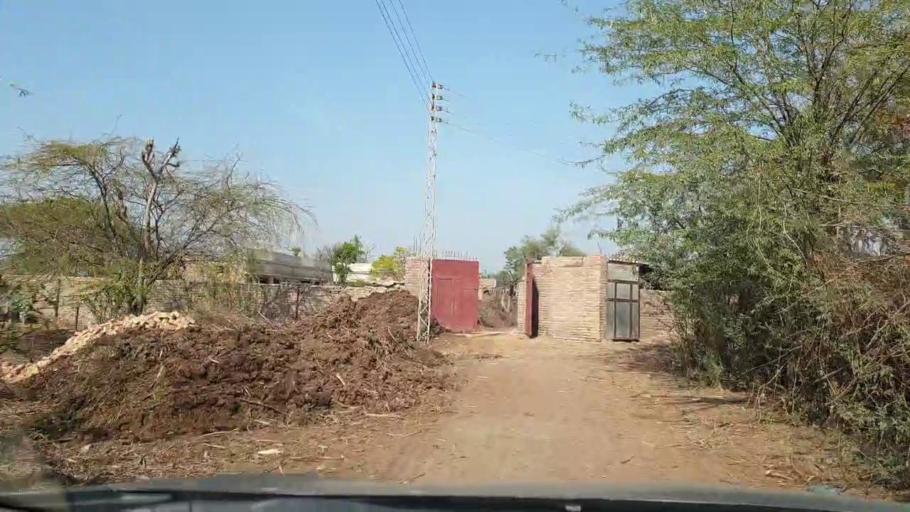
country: PK
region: Sindh
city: Berani
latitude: 25.6889
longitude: 68.7520
